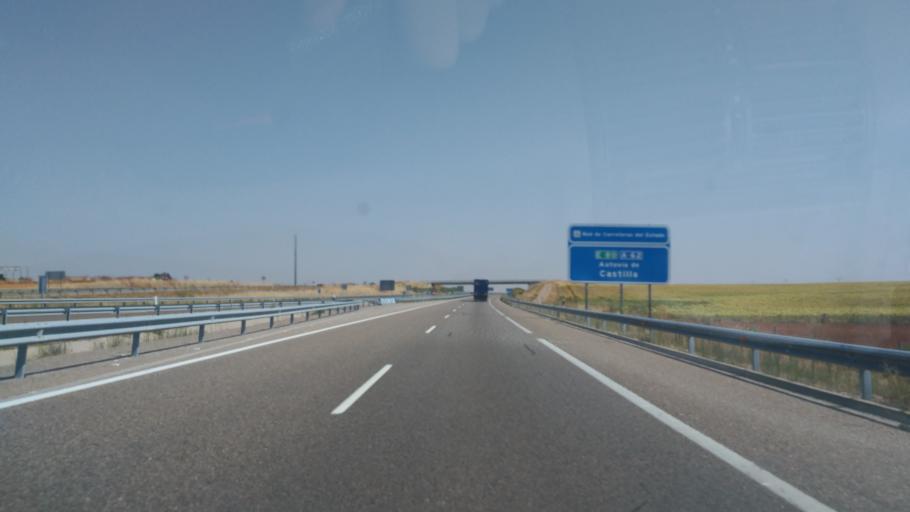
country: ES
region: Castille and Leon
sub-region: Provincia de Salamanca
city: Robliza de Cojos
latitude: 40.8797
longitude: -5.9719
